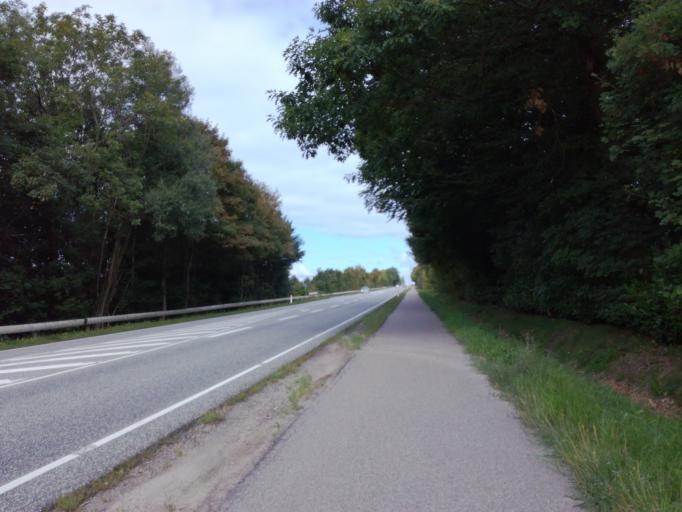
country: DK
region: South Denmark
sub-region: Vejle Kommune
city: Borkop
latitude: 55.6615
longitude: 9.5887
